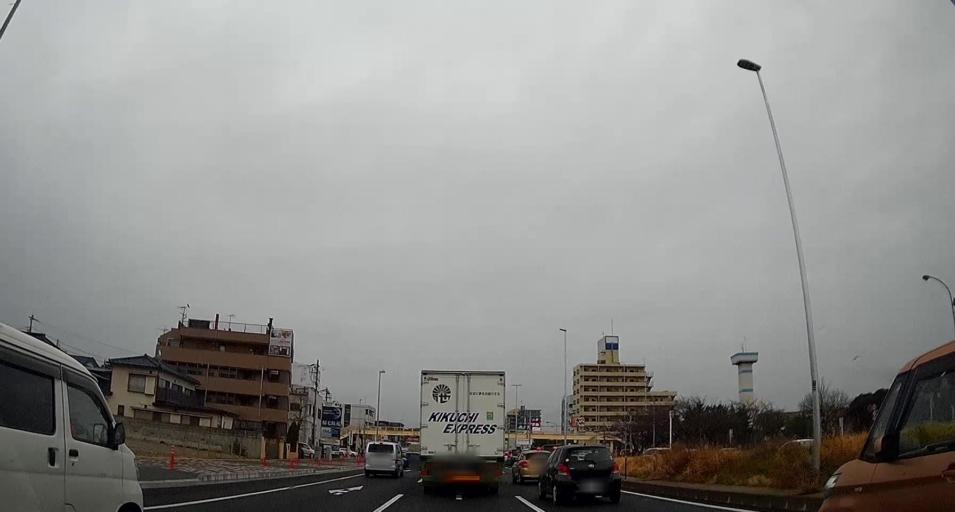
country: JP
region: Chiba
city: Chiba
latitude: 35.6369
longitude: 140.0793
